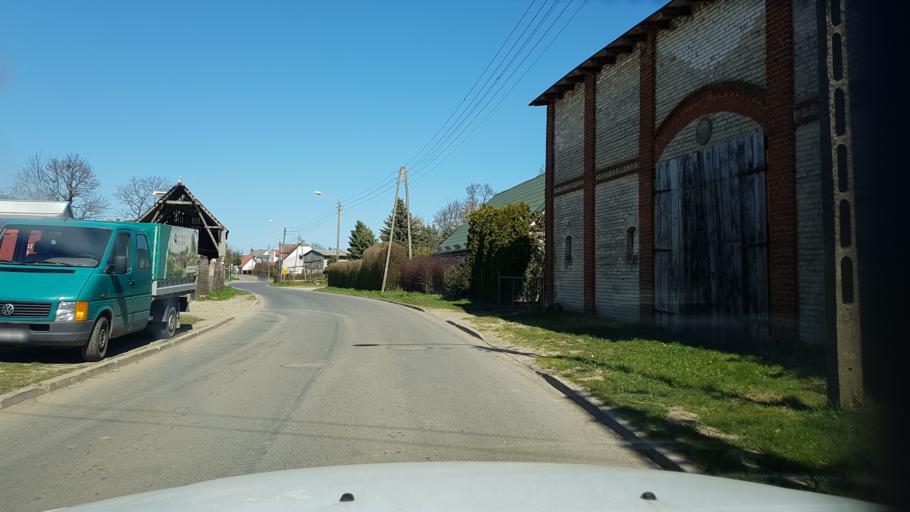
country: PL
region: West Pomeranian Voivodeship
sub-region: Koszalin
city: Koszalin
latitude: 54.2436
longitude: 16.1654
